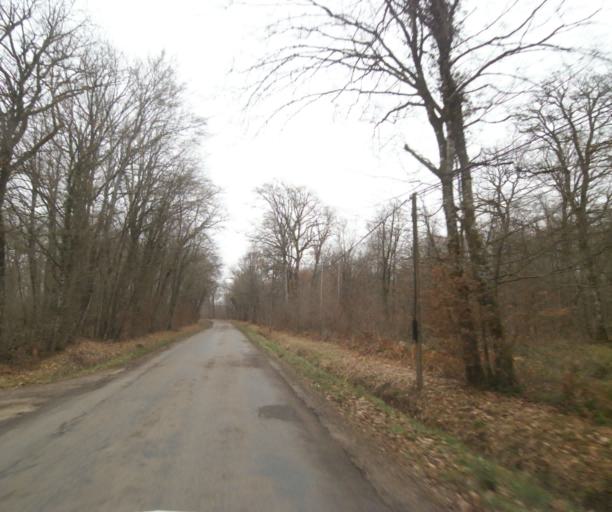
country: FR
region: Champagne-Ardenne
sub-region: Departement de la Haute-Marne
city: Wassy
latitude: 48.5281
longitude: 4.9775
